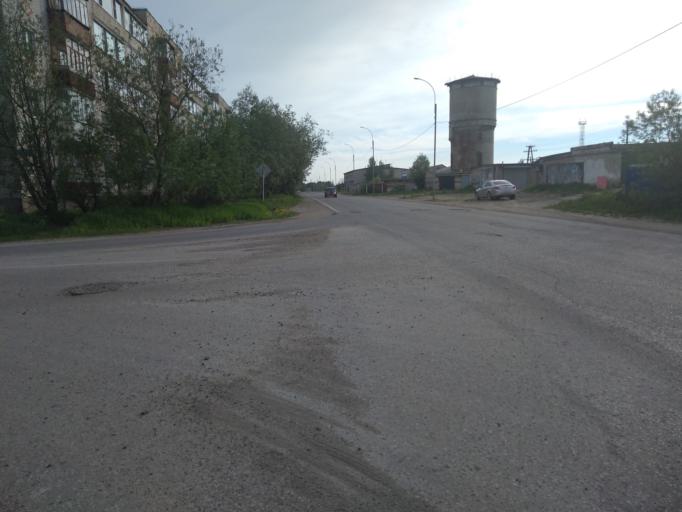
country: RU
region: Komi Republic
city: Pechora
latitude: 65.1484
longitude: 57.2140
